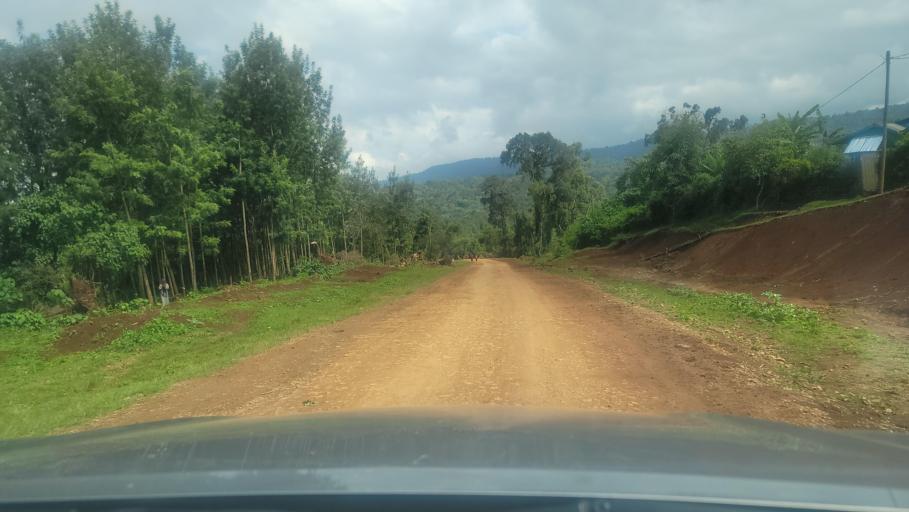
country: ET
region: Oromiya
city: Agaro
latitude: 7.7922
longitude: 36.4388
